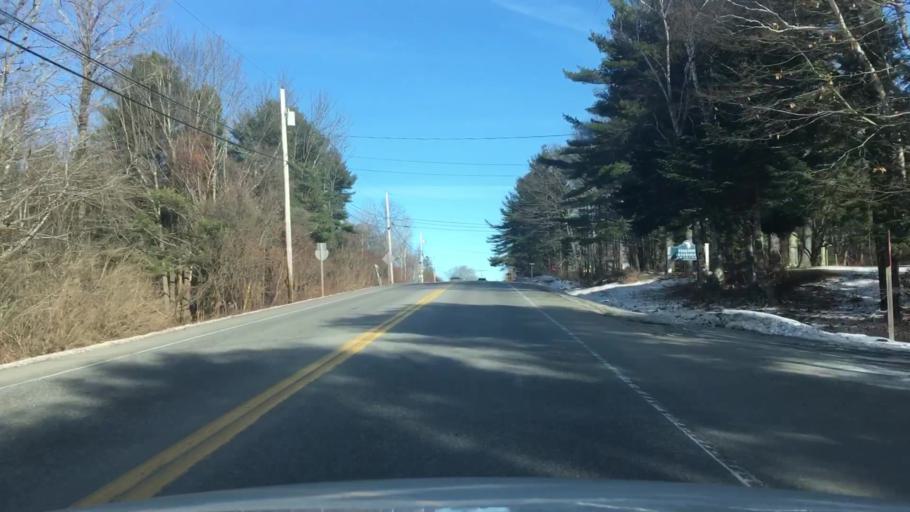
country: US
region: Maine
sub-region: Cumberland County
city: Freeport
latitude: 43.8670
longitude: -70.1092
